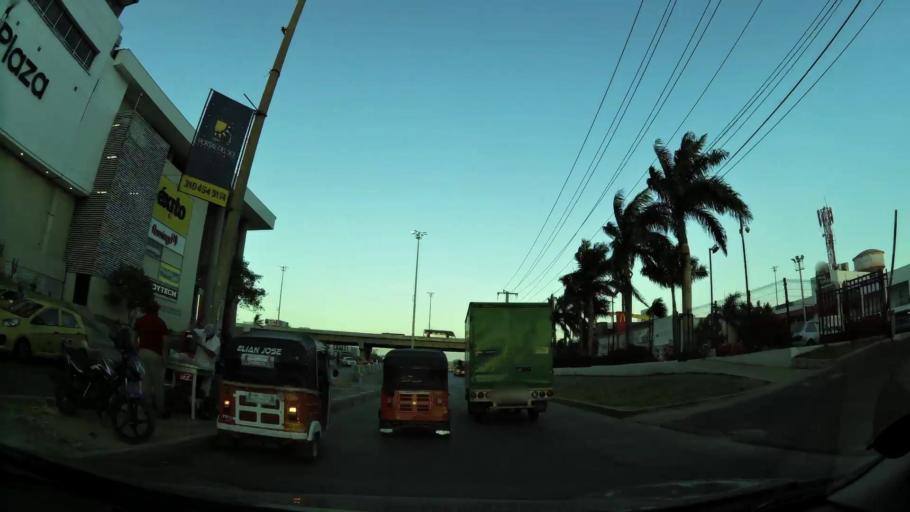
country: CO
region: Atlantico
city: Soledad
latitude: 10.9264
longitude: -74.7798
